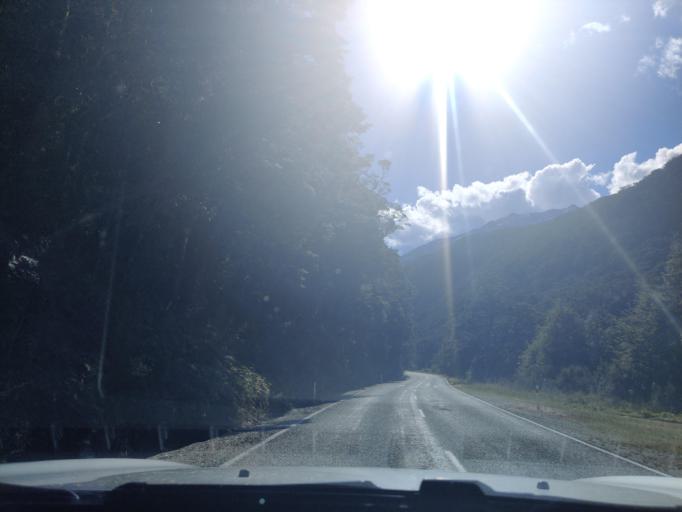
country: NZ
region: Otago
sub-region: Queenstown-Lakes District
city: Wanaka
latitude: -44.0953
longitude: 169.3638
